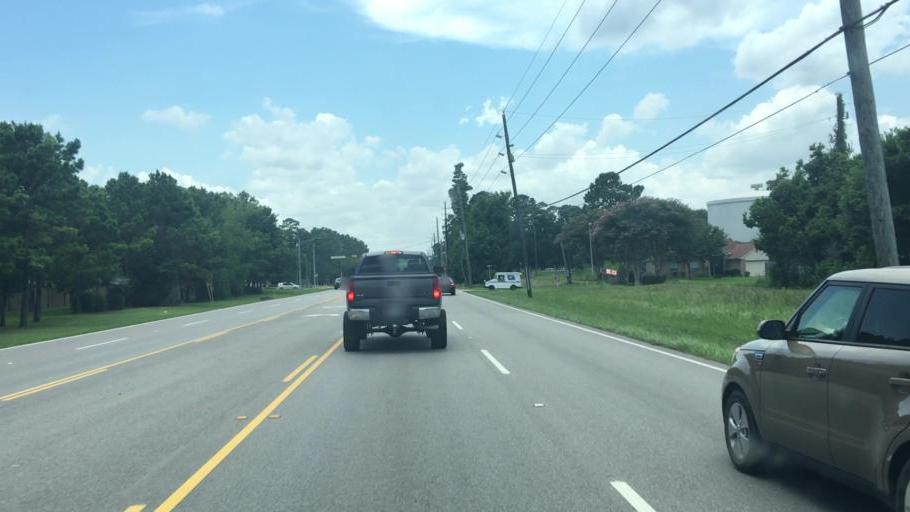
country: US
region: Texas
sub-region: Harris County
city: Atascocita
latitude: 29.9917
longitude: -95.1830
